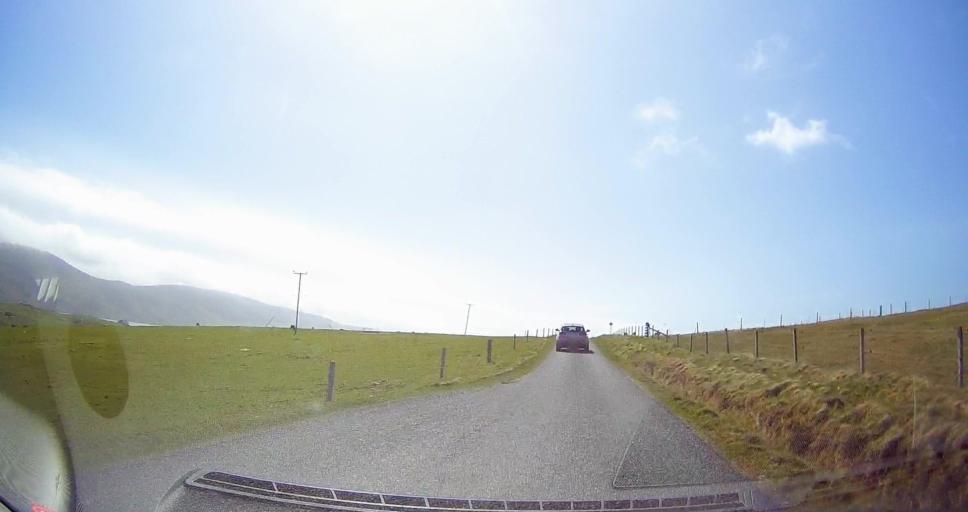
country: GB
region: Scotland
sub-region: Shetland Islands
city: Sandwick
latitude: 60.0763
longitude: -1.3383
